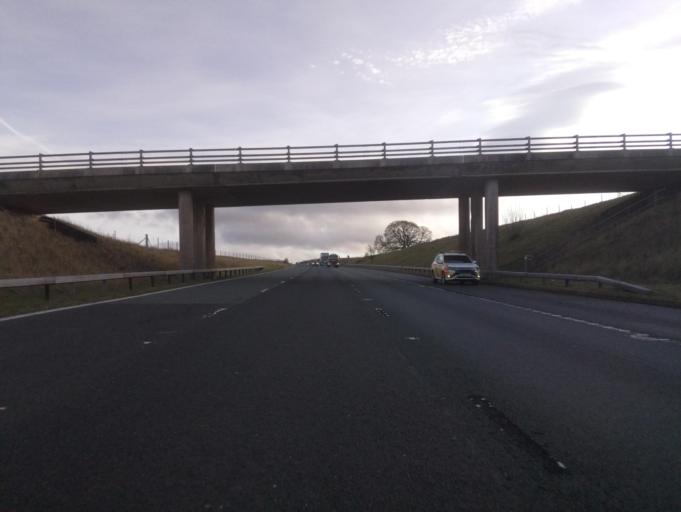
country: GB
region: England
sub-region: Cumbria
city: Penrith
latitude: 54.5472
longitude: -2.6694
